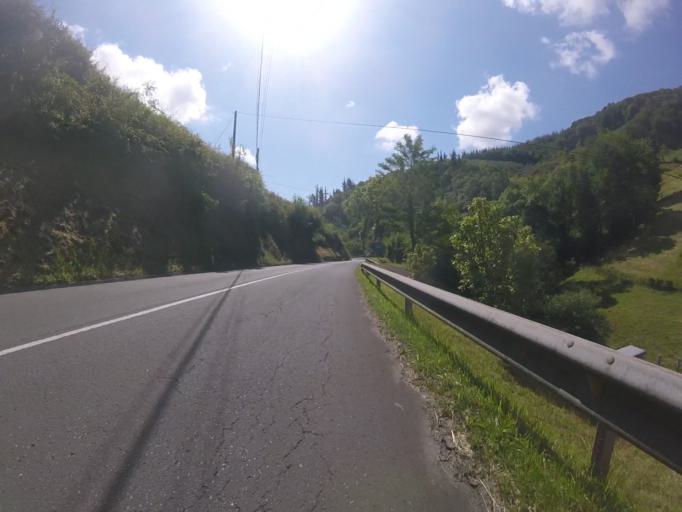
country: ES
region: Basque Country
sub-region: Provincia de Guipuzcoa
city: Azpeitia
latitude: 43.1797
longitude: -2.2305
